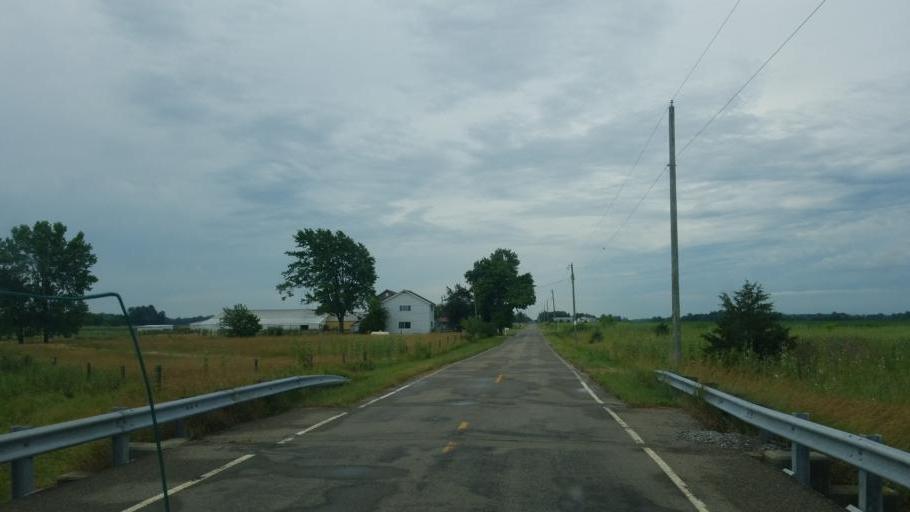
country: US
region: Ohio
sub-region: Defiance County
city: Hicksville
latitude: 41.2741
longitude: -84.6895
